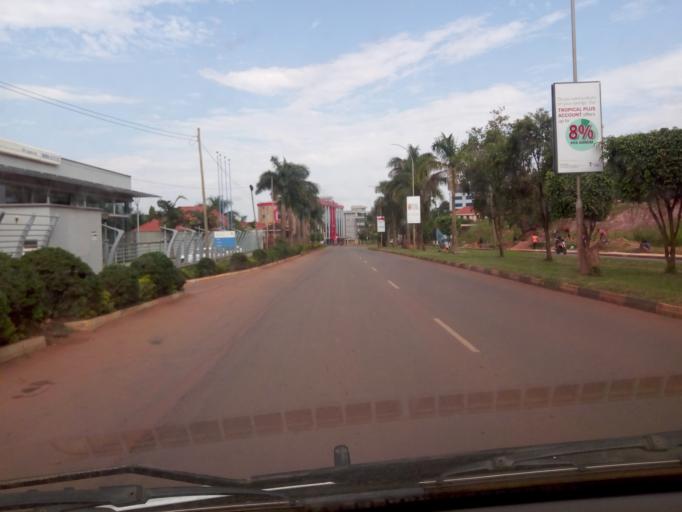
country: UG
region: Central Region
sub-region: Kampala District
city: Kampala
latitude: 0.3368
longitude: 32.6004
